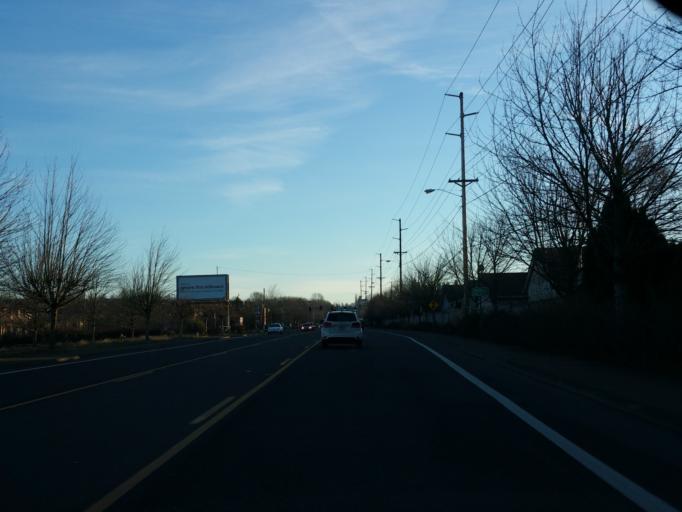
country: US
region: Oregon
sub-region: Multnomah County
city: Fairview
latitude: 45.5320
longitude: -122.4337
